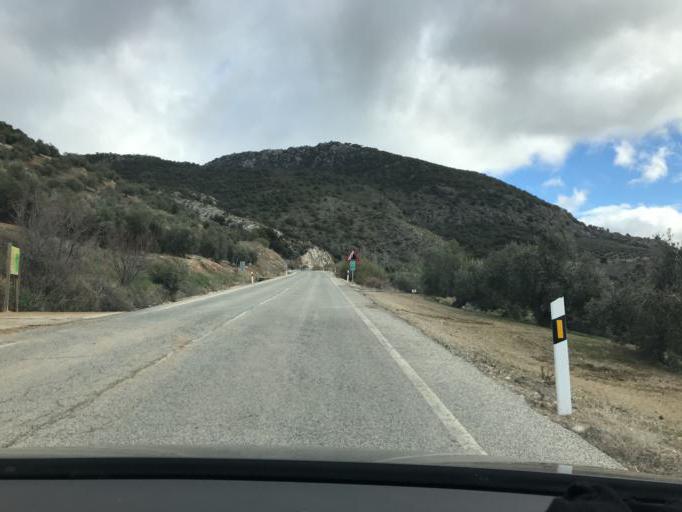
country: ES
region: Andalusia
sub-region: Provincia de Jaen
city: Cambil
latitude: 37.6925
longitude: -3.5164
